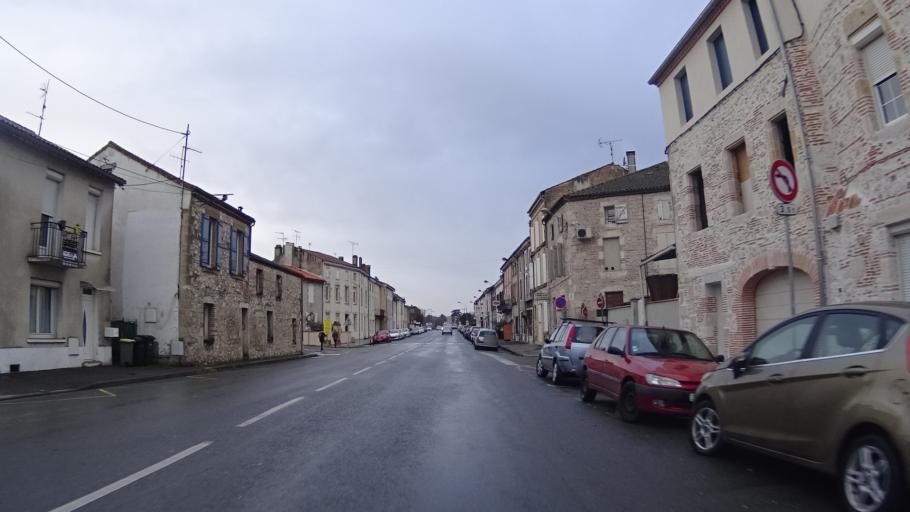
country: FR
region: Aquitaine
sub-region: Departement du Lot-et-Garonne
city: Le Passage
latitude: 44.1942
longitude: 0.6074
